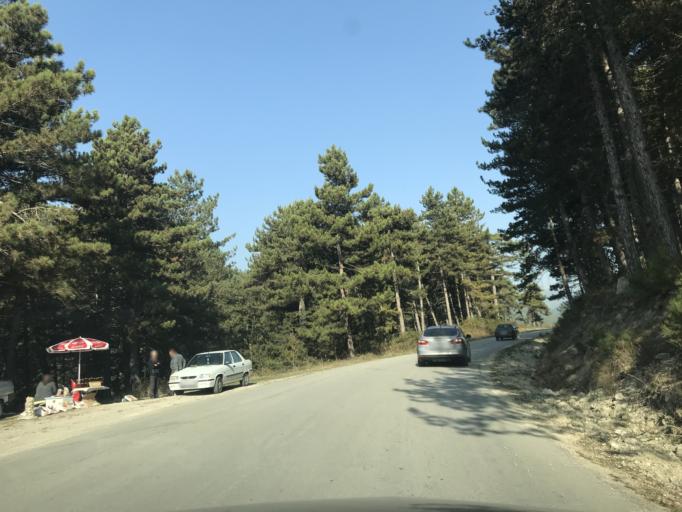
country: TR
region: Bolu
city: Bolu
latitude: 40.7849
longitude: 31.6326
